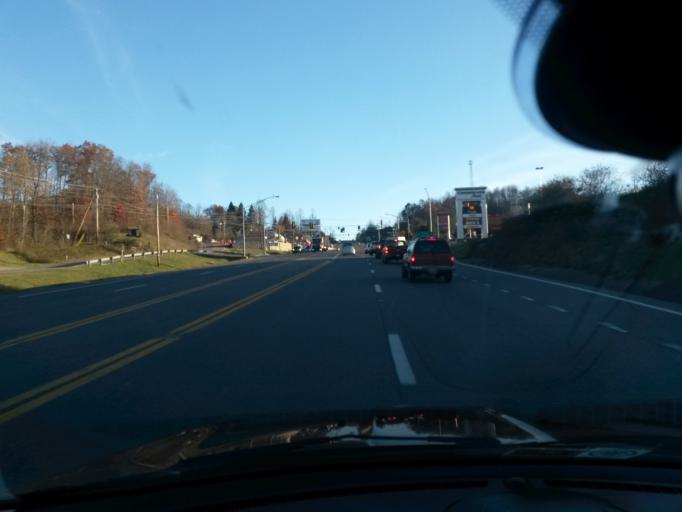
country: US
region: West Virginia
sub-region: Raleigh County
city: Prosperity
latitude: 37.8491
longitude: -81.1962
